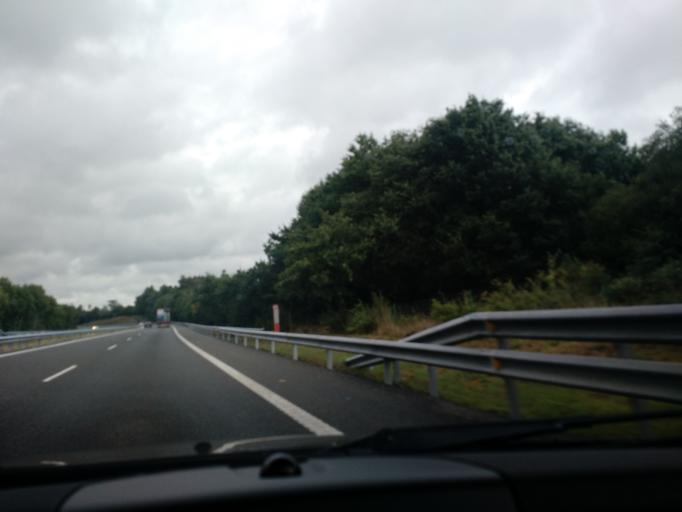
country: ES
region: Galicia
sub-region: Provincia da Coruna
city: Oroso
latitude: 42.9994
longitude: -8.4233
